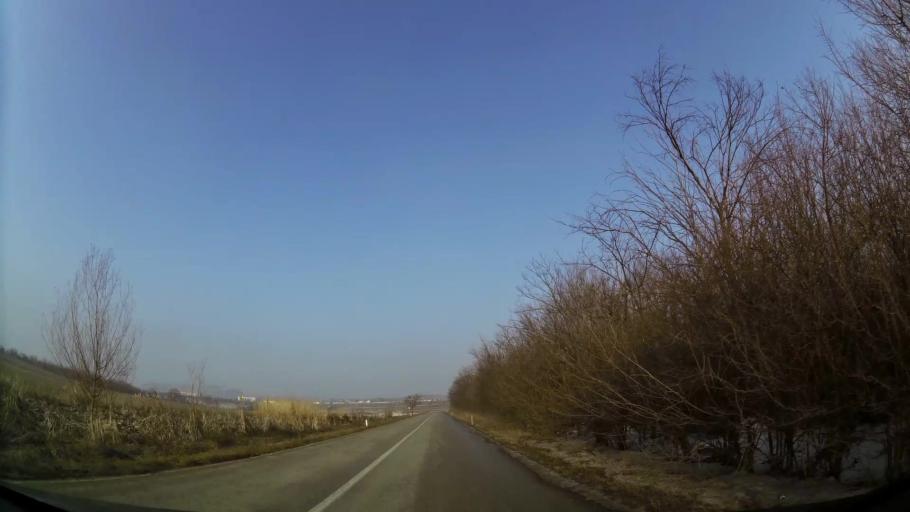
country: MK
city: Kadino
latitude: 41.9767
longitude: 21.6111
